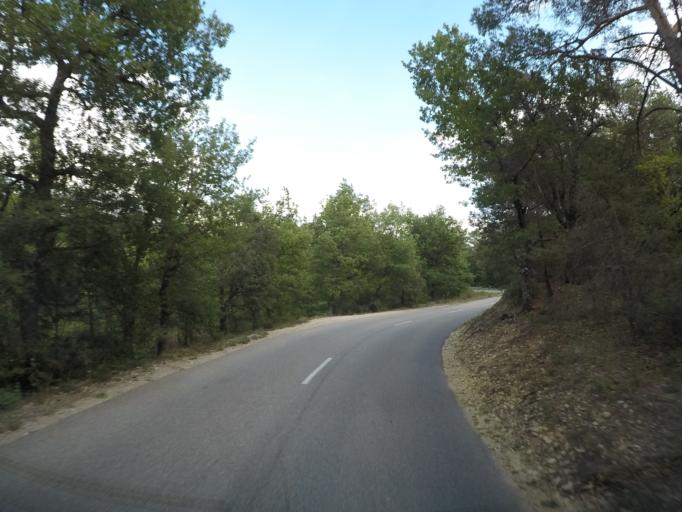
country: FR
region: Provence-Alpes-Cote d'Azur
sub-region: Departement des Alpes-de-Haute-Provence
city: Valensole
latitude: 43.8338
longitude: 6.0086
